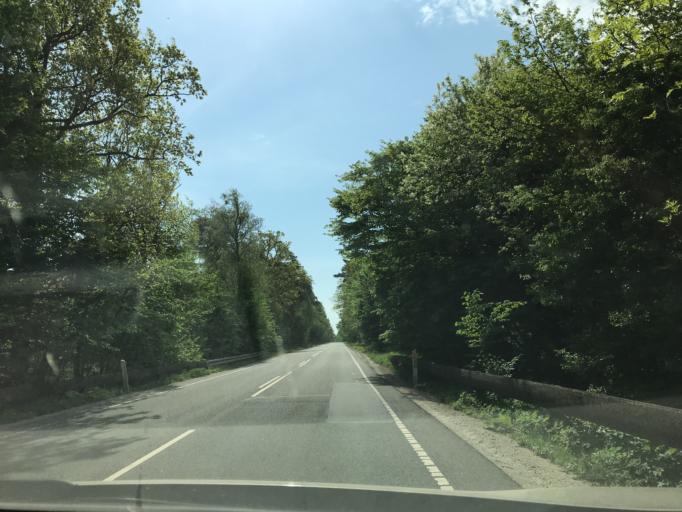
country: DK
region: South Denmark
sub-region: Middelfart Kommune
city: Ejby
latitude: 55.3962
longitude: 9.9064
